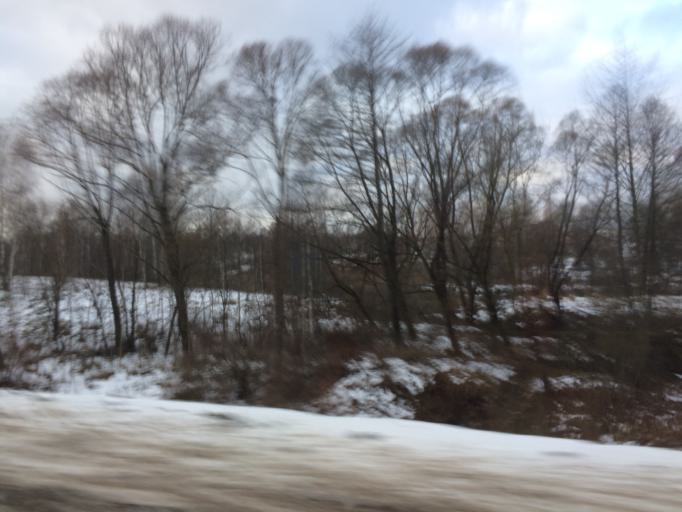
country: RU
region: Tula
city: Ageyevo
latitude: 54.1248
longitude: 36.4525
